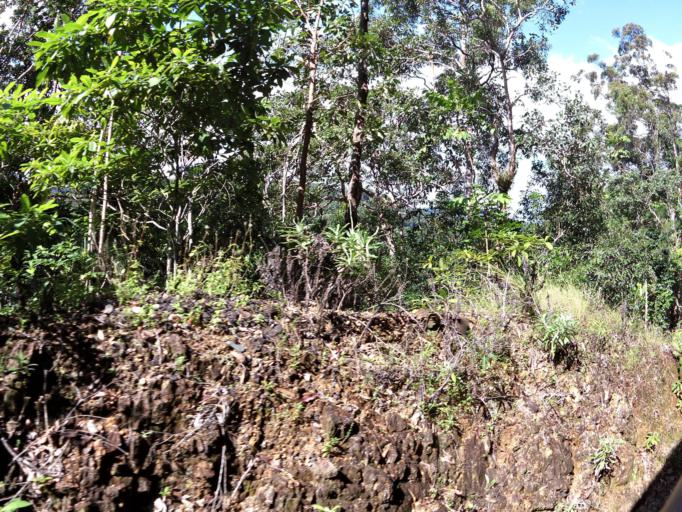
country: AU
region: Queensland
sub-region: Tablelands
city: Kuranda
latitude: -16.8334
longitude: 145.6421
